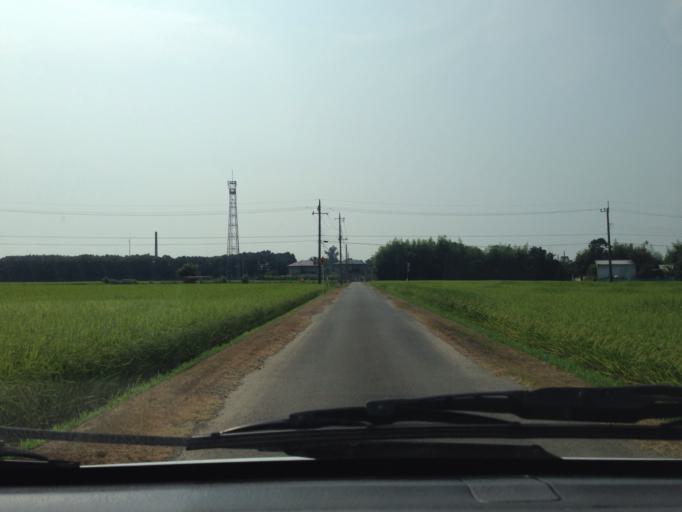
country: JP
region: Ibaraki
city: Inashiki
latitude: 36.0077
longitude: 140.3690
